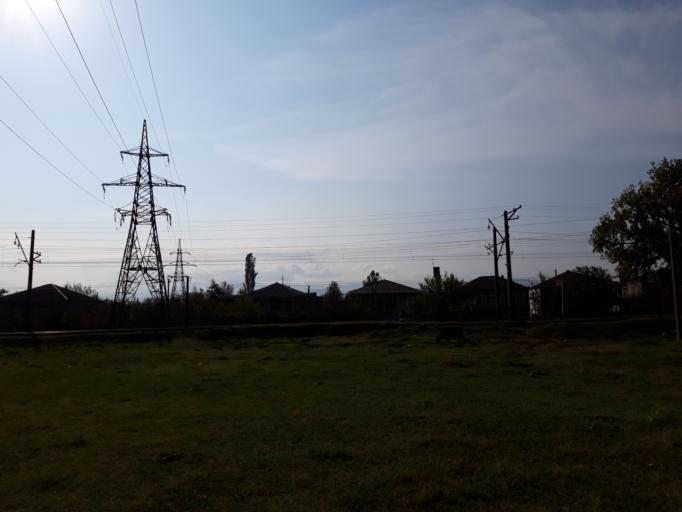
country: GE
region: Imereti
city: Samtredia
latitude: 42.1572
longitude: 42.3245
